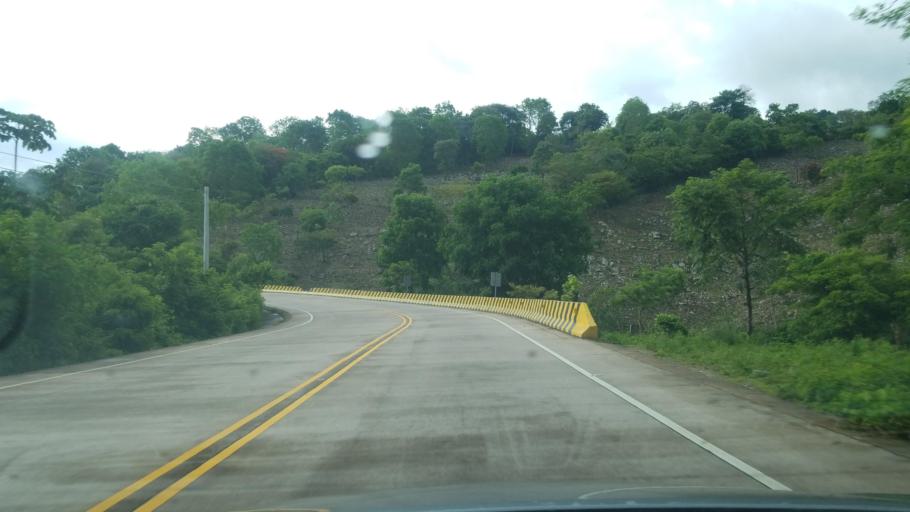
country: HN
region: Copan
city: Copan
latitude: 14.8415
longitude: -89.1863
